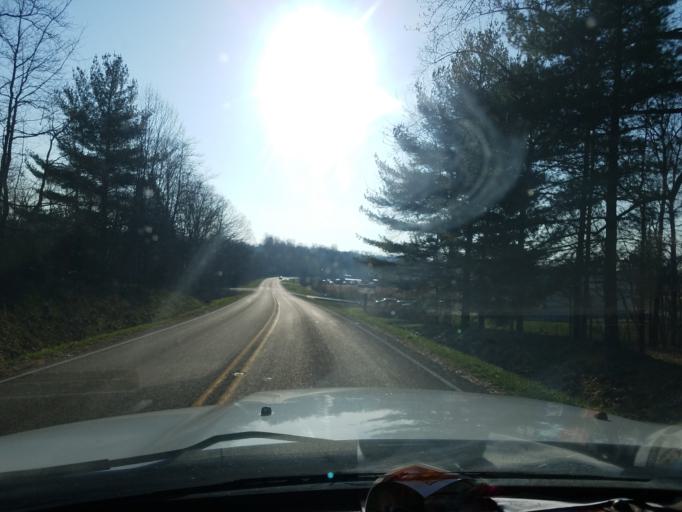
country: US
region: Indiana
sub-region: Owen County
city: Spencer
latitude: 39.3420
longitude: -86.9036
